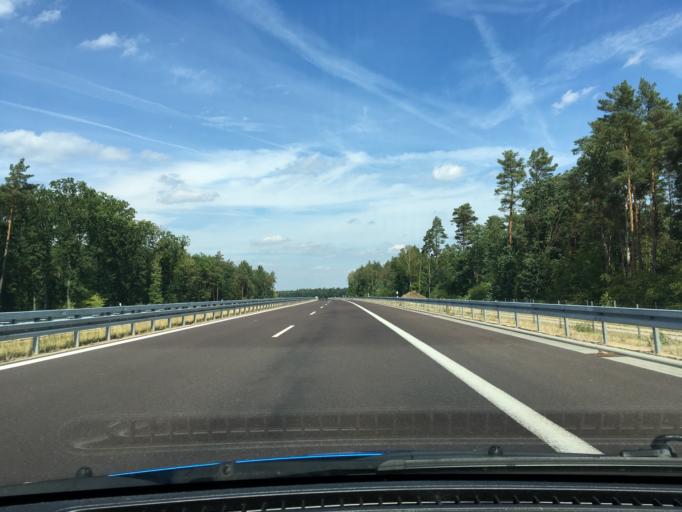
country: DE
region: Mecklenburg-Vorpommern
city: Ludwigslust
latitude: 53.3218
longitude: 11.5281
